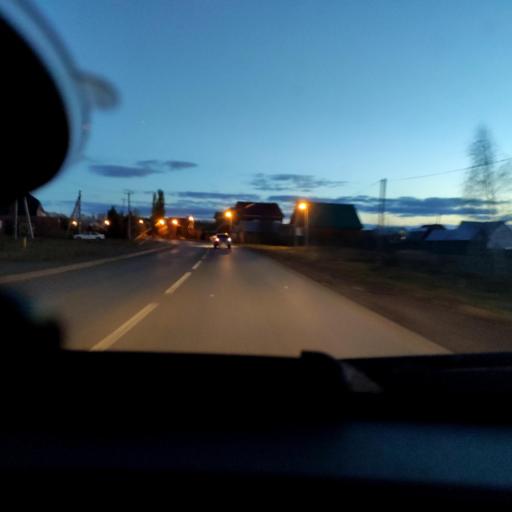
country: RU
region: Bashkortostan
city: Avdon
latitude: 54.6974
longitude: 55.7960
